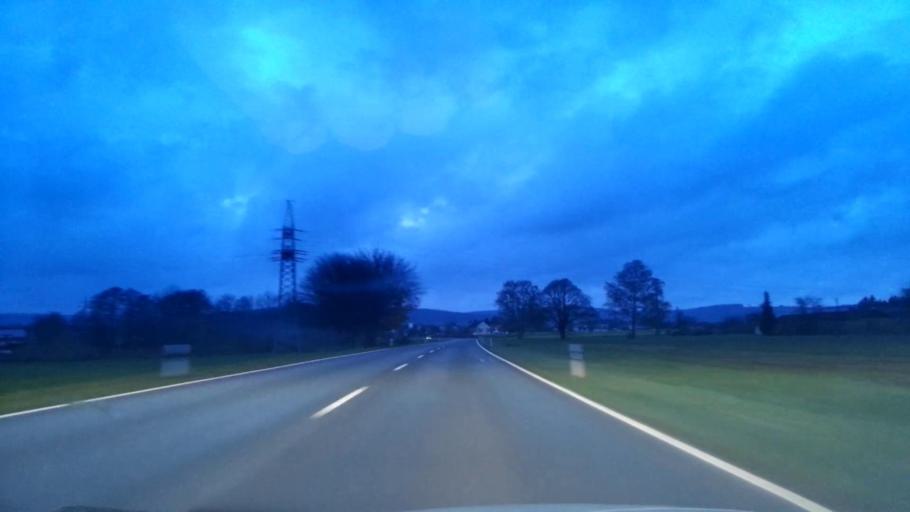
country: DE
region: Bavaria
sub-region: Upper Palatinate
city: Immenreuth
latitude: 49.8989
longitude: 11.8729
